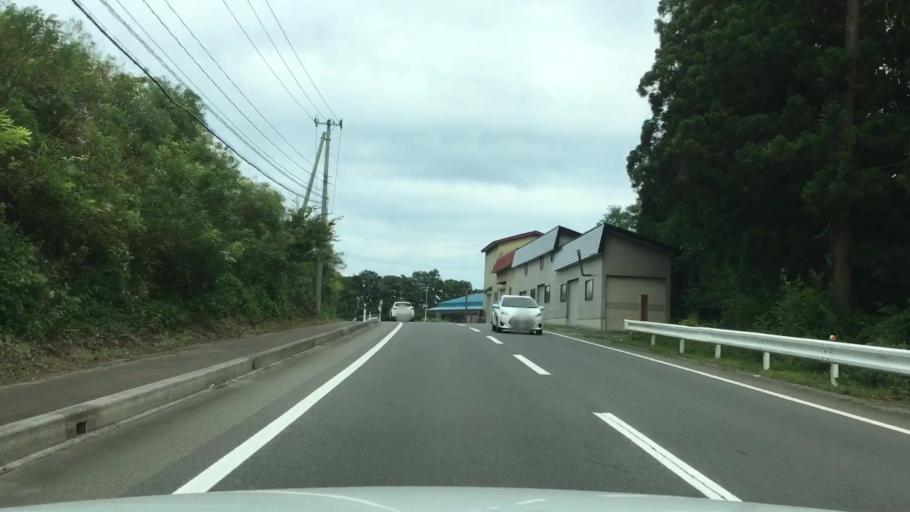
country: JP
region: Aomori
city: Shimokizukuri
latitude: 40.7652
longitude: 140.2247
